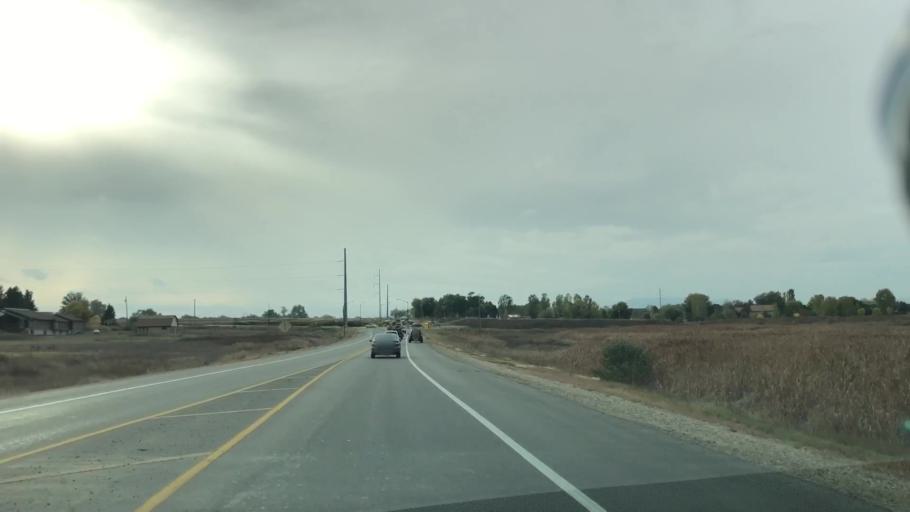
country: US
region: Colorado
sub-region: Larimer County
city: Loveland
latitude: 40.4657
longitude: -105.0406
